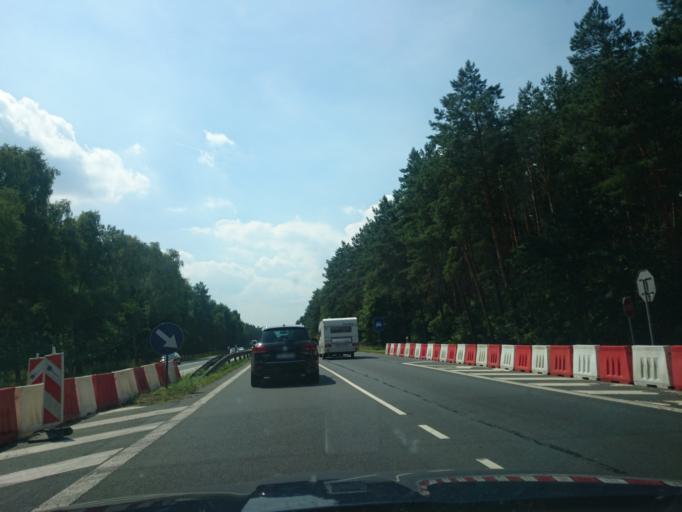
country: PL
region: West Pomeranian Voivodeship
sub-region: Powiat stargardzki
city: Kobylanka
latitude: 53.4359
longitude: 14.7767
